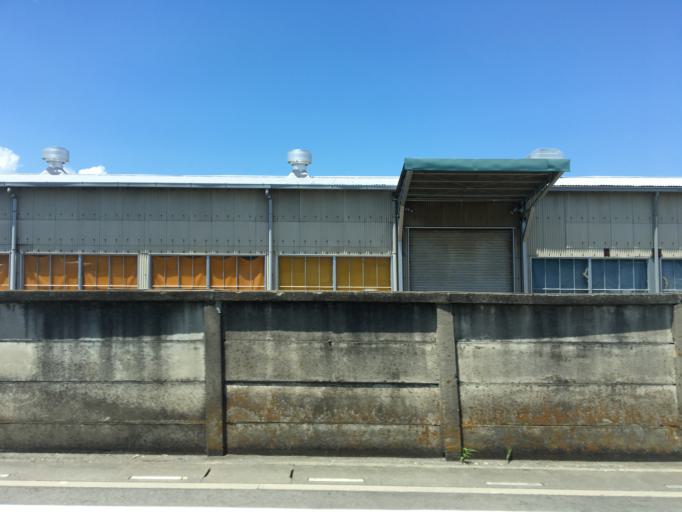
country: JP
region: Saitama
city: Sakado
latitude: 35.9413
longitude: 139.4002
